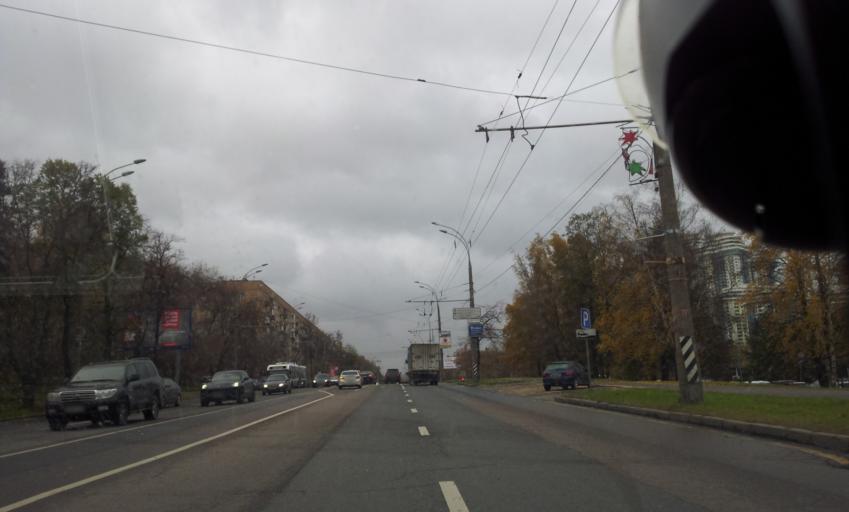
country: RU
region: Moscow
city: Vorob'yovo
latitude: 55.7178
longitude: 37.5194
